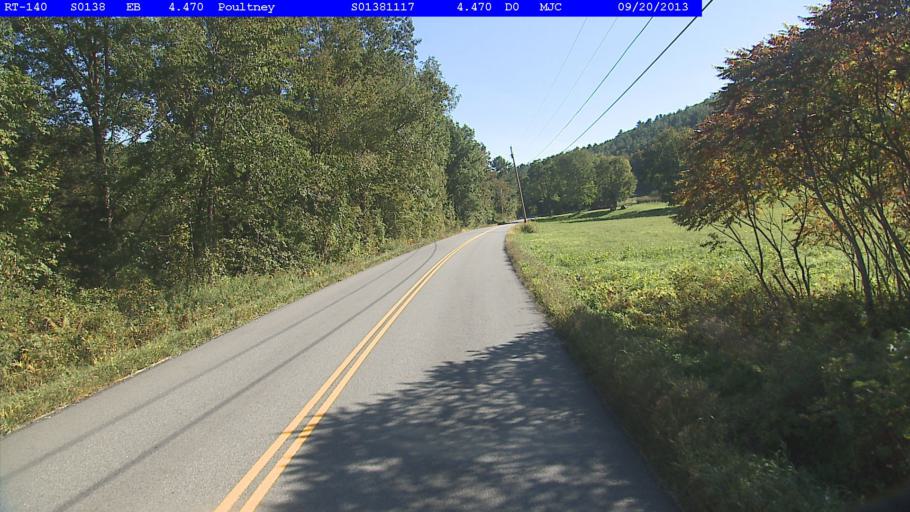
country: US
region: Vermont
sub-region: Rutland County
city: Poultney
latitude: 43.5020
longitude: -73.1751
